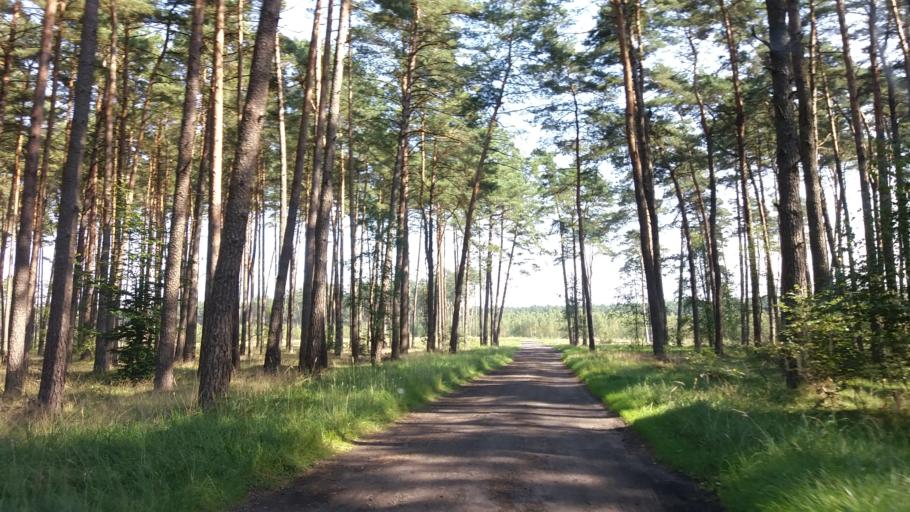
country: PL
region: West Pomeranian Voivodeship
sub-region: Powiat walecki
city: Tuczno
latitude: 53.2173
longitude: 16.0201
